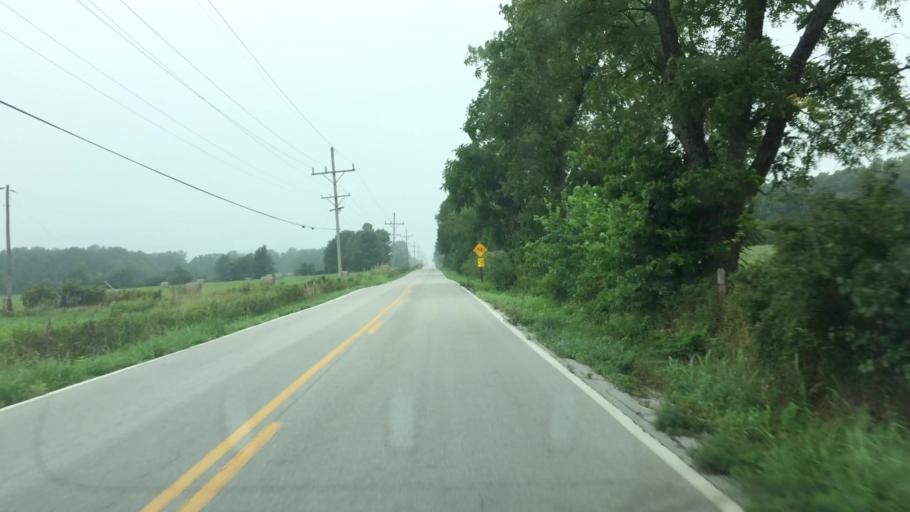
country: US
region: Missouri
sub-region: Greene County
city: Strafford
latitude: 37.2710
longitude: -93.1380
